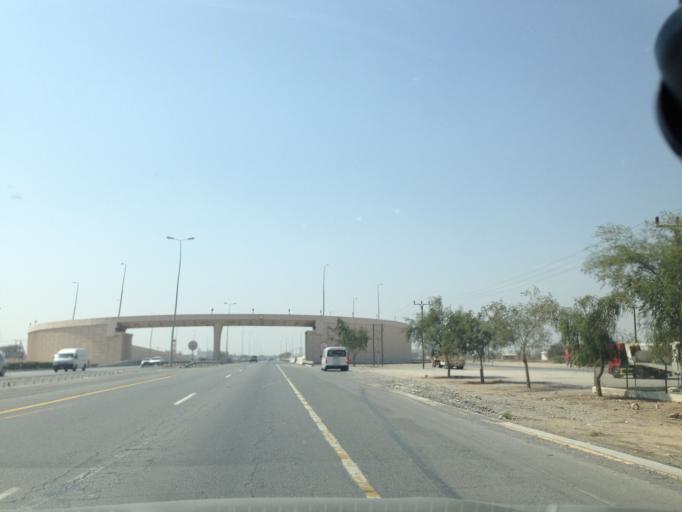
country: OM
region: Al Batinah
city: Barka'
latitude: 23.6636
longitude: 57.9493
